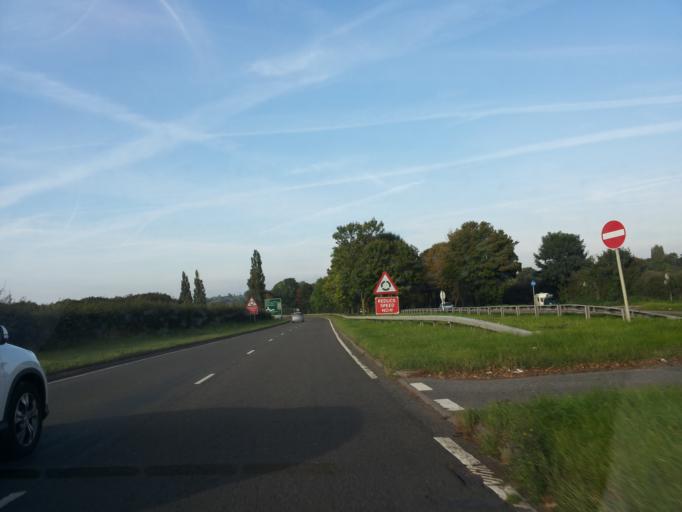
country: GB
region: England
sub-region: Staffordshire
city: Stone
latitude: 52.8820
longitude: -2.1336
